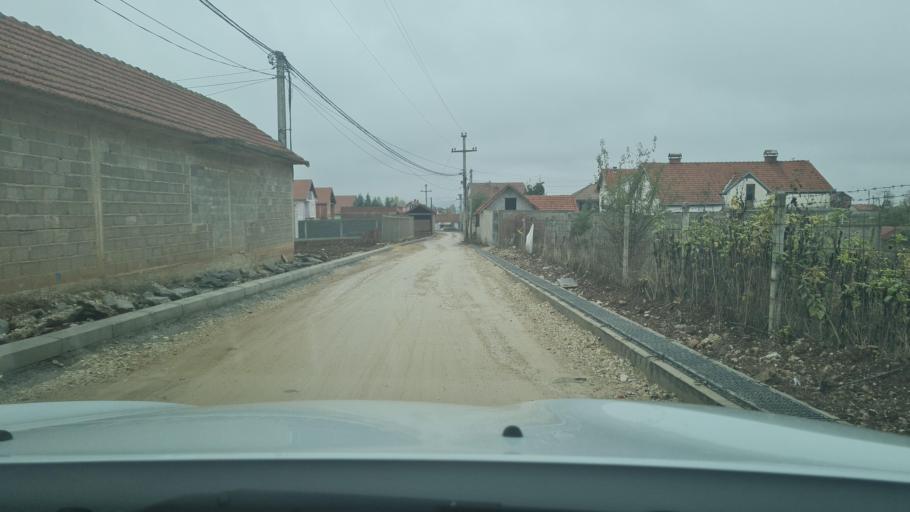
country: MK
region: Opstina Lipkovo
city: Matejche
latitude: 42.1078
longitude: 21.6190
